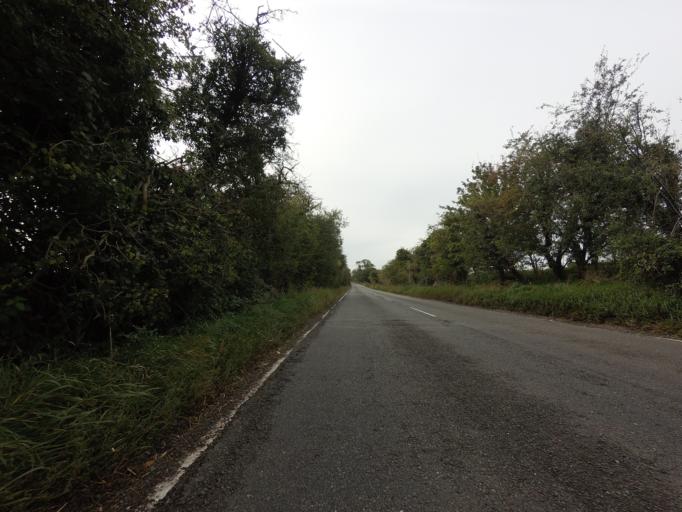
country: GB
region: England
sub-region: Cambridgeshire
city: Melbourn
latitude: 52.0390
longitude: 0.0423
